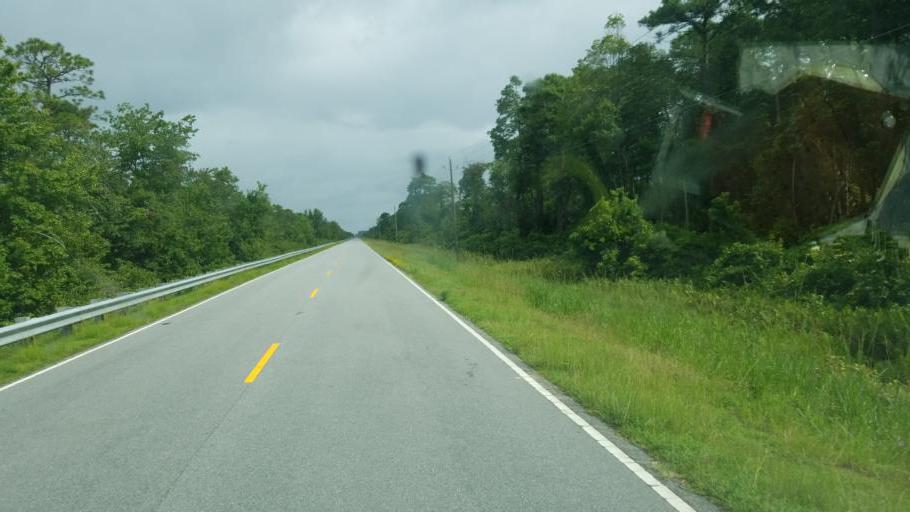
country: US
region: North Carolina
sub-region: Dare County
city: Wanchese
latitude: 35.7396
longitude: -75.7687
